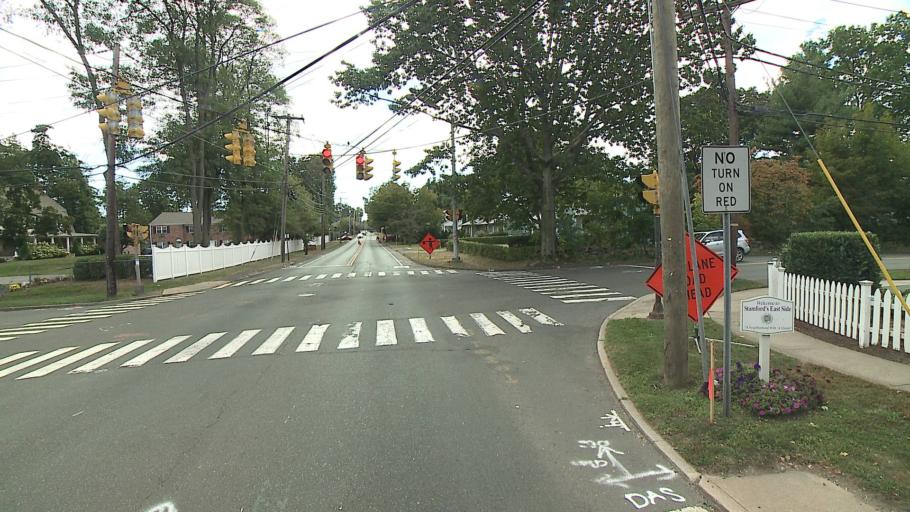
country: US
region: Connecticut
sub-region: Fairfield County
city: Stamford
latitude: 41.0641
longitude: -73.5150
